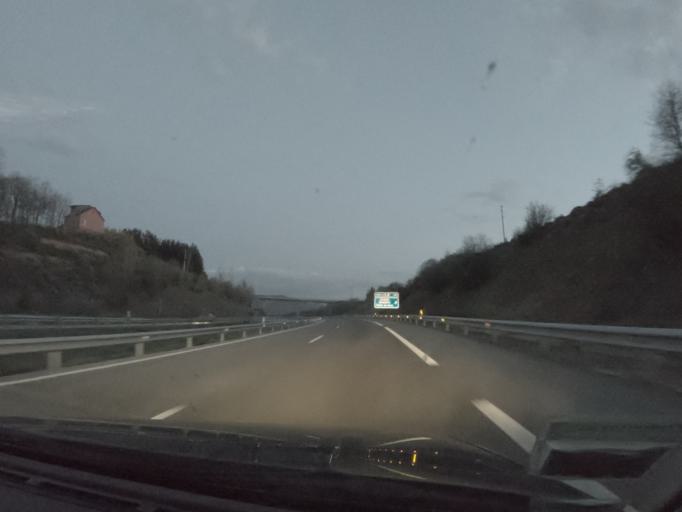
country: ES
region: Castille and Leon
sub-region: Provincia de Leon
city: Bembibre
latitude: 42.6177
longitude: -6.4051
